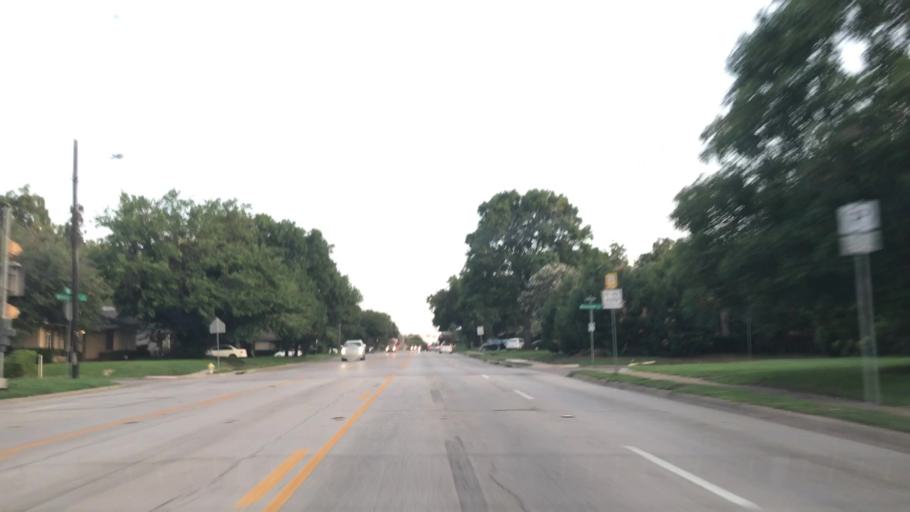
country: US
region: Texas
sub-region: Dallas County
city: Highland Park
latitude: 32.8404
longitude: -96.7615
